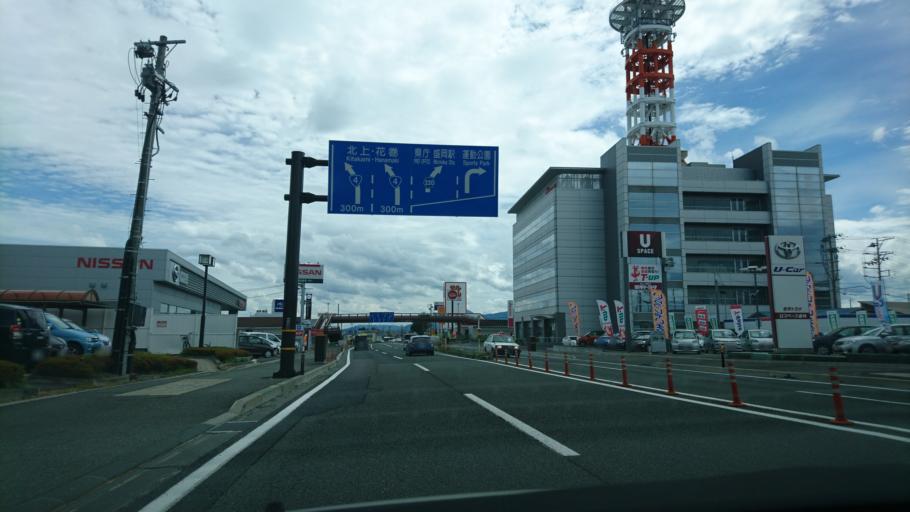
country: JP
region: Iwate
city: Morioka-shi
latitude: 39.7303
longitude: 141.1232
